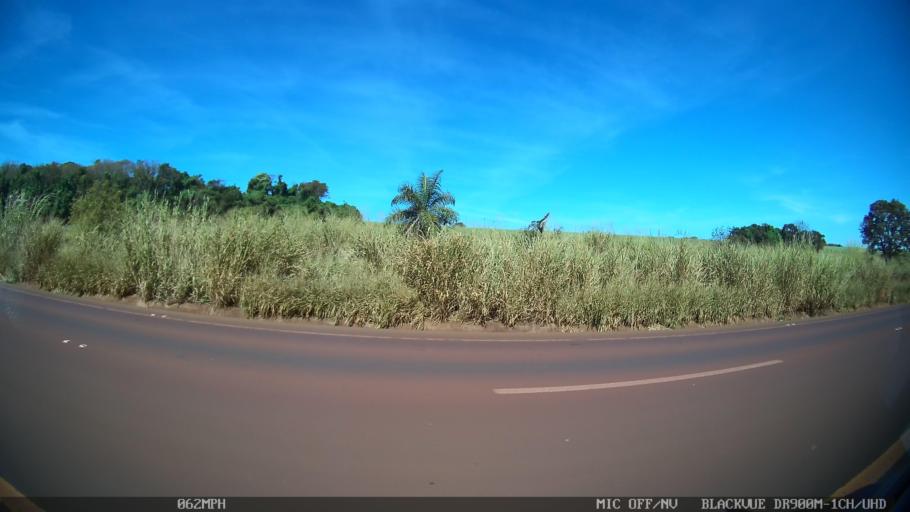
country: BR
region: Sao Paulo
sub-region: Sao Joaquim Da Barra
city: Sao Joaquim da Barra
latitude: -20.5512
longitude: -47.6562
